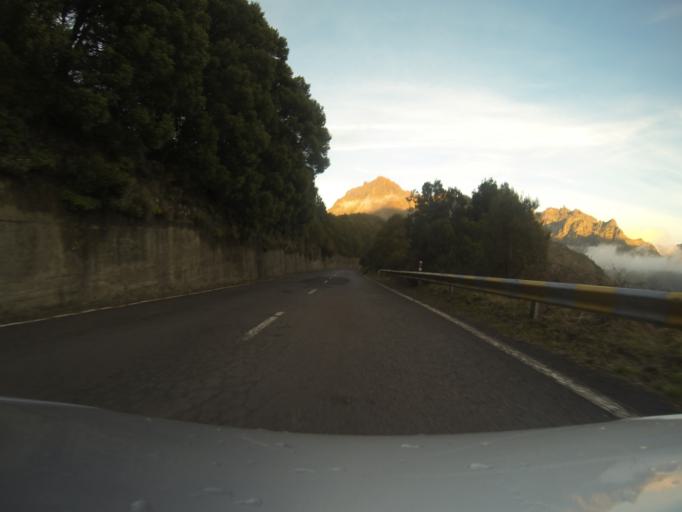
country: PT
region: Madeira
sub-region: Sao Vicente
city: Sao Vicente
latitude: 32.7548
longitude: -17.0221
